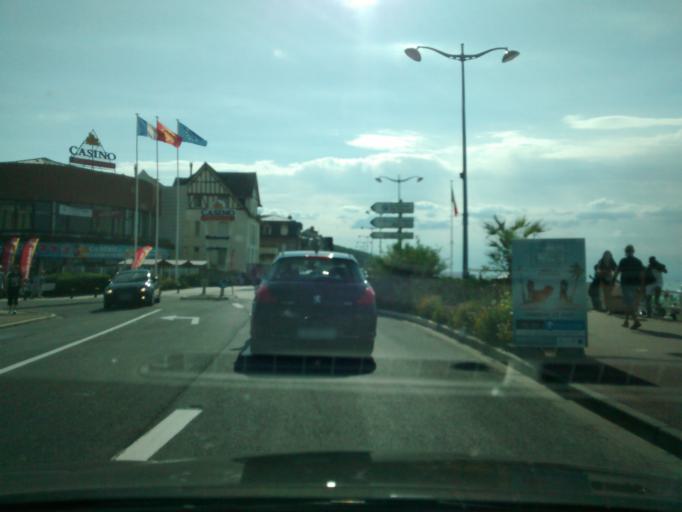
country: FR
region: Lower Normandy
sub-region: Departement du Calvados
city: Villers-sur-Mer
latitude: 49.3253
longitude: -0.0009
